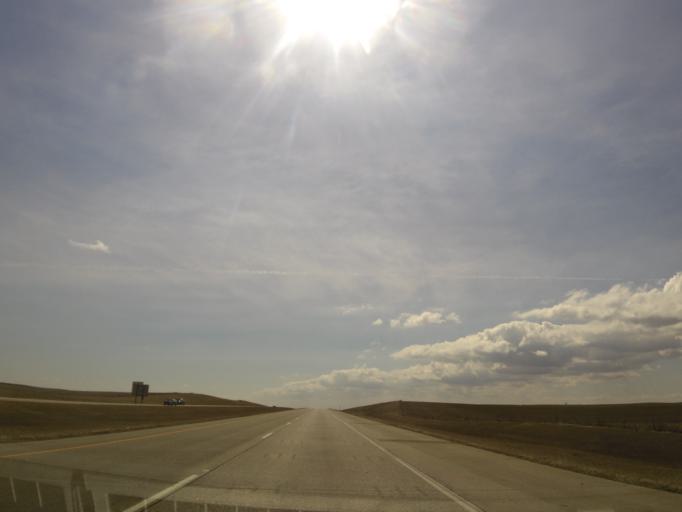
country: US
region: South Dakota
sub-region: Roberts County
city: Sisseton
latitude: 45.6420
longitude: -96.9897
